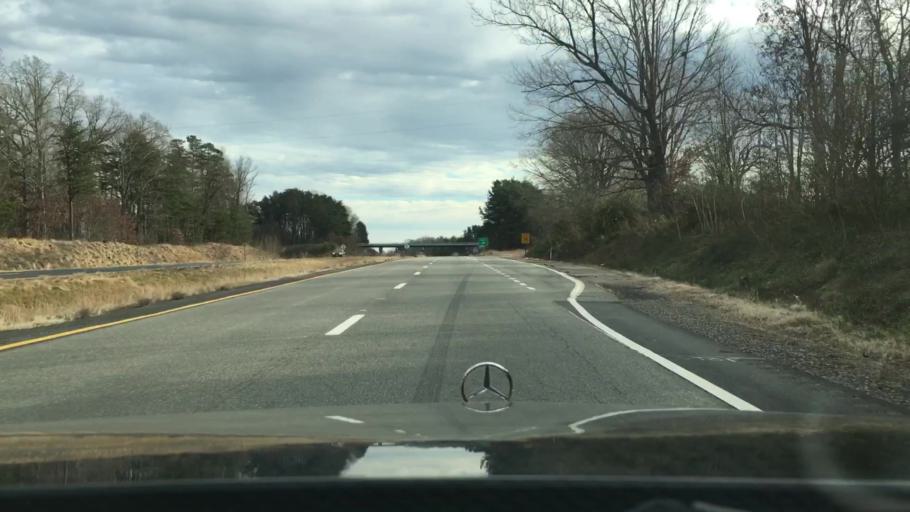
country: US
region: Virginia
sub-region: Pittsylvania County
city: Chatham
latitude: 36.8522
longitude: -79.3956
